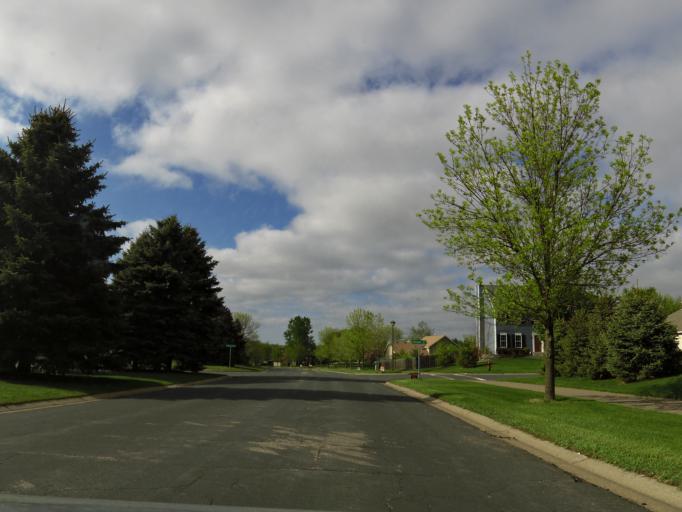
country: US
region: Minnesota
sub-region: Washington County
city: Woodbury
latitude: 44.9218
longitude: -92.9175
